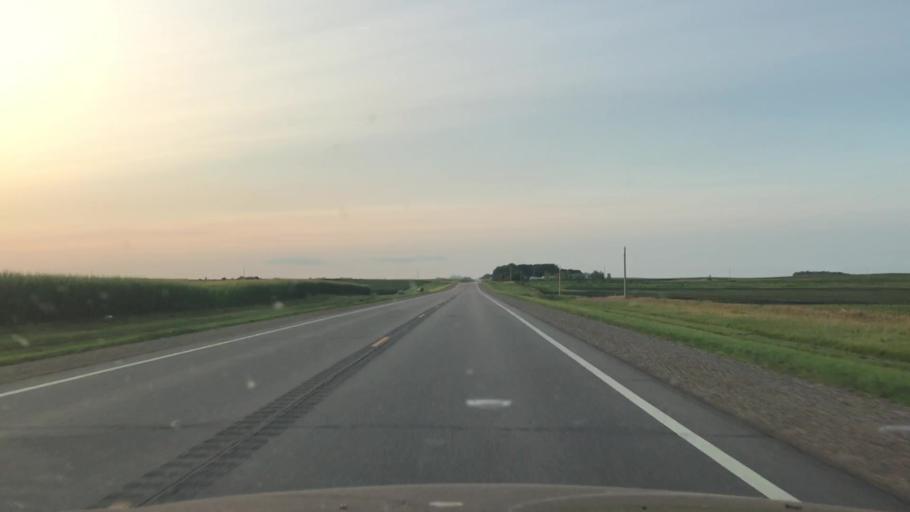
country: US
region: Minnesota
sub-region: Redwood County
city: Redwood Falls
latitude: 44.4368
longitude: -95.1176
